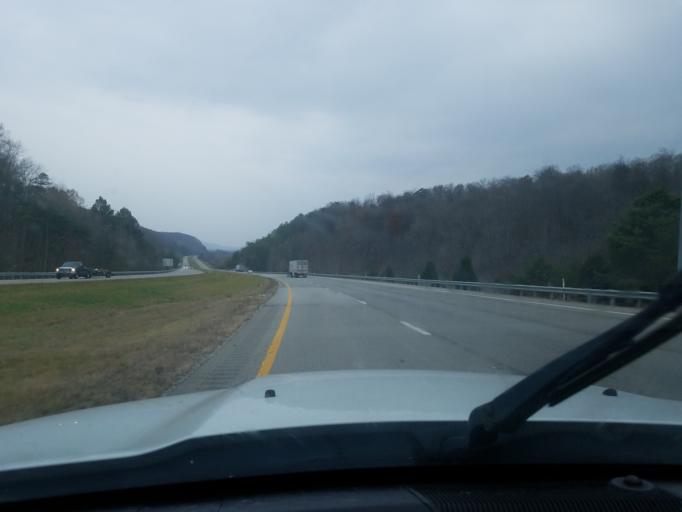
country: US
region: Kentucky
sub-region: Rowan County
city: Morehead
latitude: 38.1819
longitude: -83.5644
